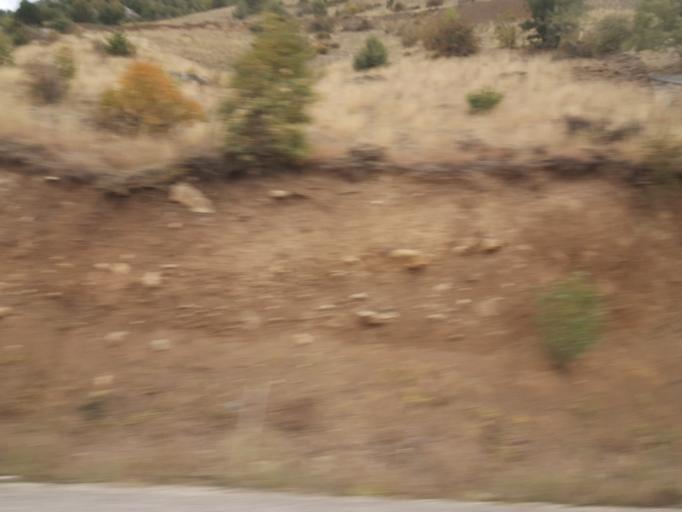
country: TR
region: Yozgat
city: Cekerek
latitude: 40.2107
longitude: 35.4912
